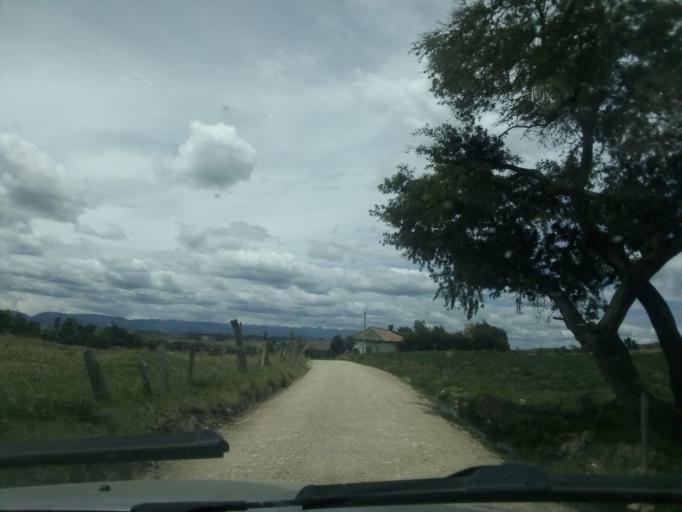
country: CO
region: Boyaca
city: Toca
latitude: 5.6020
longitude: -73.1542
